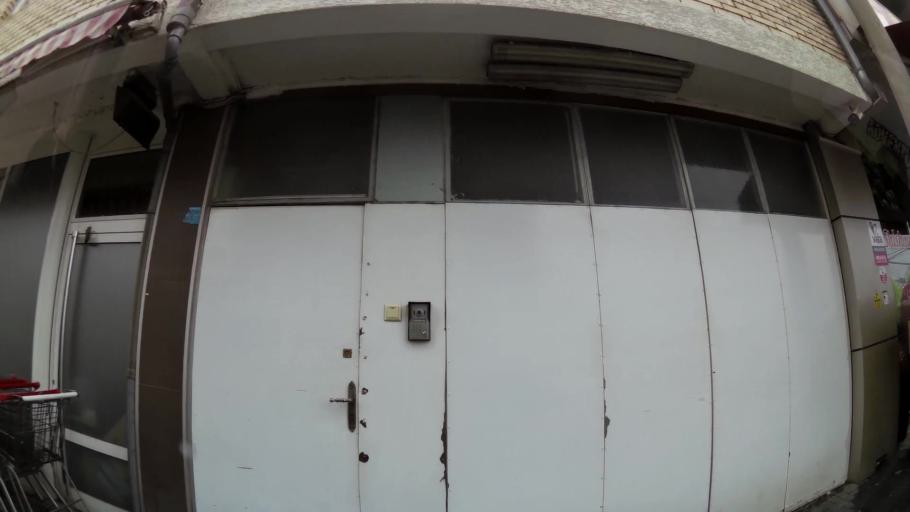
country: XK
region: Pristina
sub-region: Komuna e Prishtines
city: Pristina
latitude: 42.6755
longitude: 21.1690
